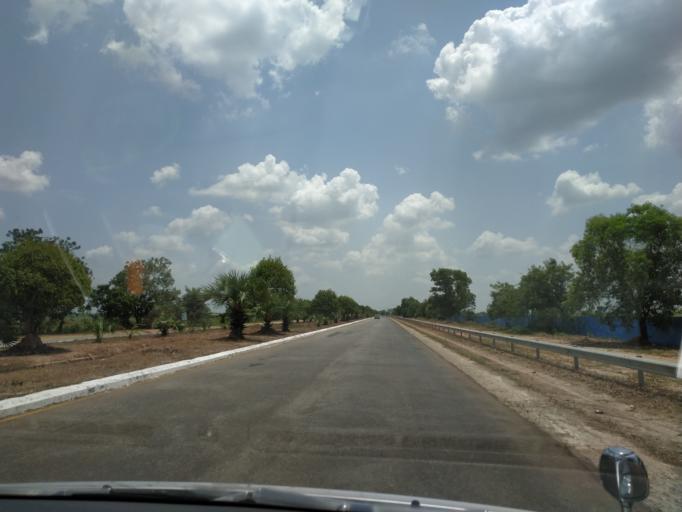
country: MM
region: Bago
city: Thanatpin
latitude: 17.1213
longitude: 96.1920
